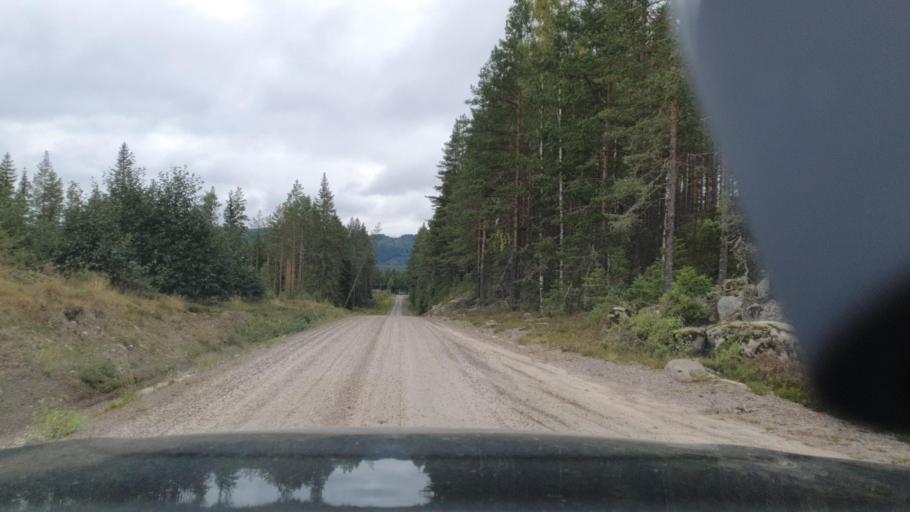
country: SE
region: Vaermland
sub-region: Torsby Kommun
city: Torsby
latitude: 60.4438
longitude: 12.9040
